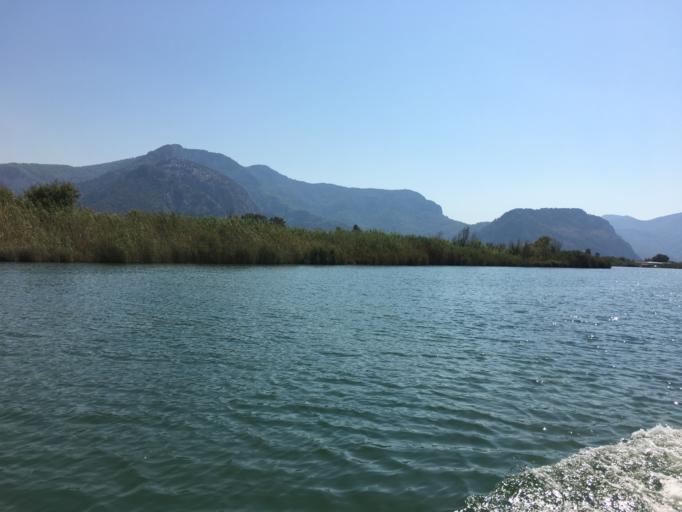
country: TR
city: Dalyan
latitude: 36.8222
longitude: 28.6348
